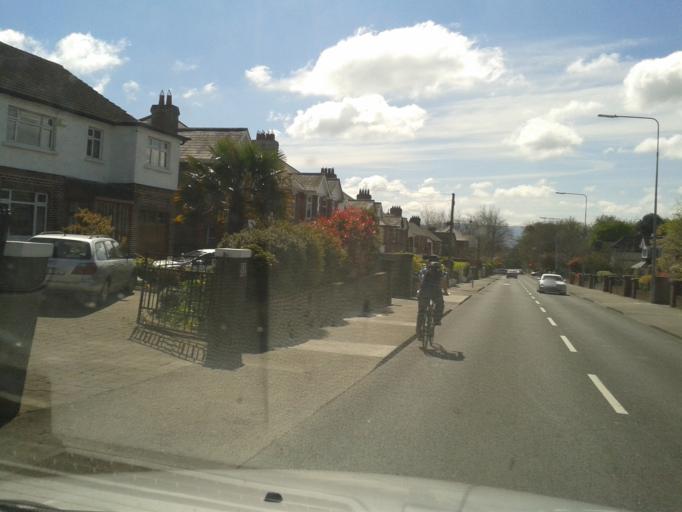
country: IE
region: Leinster
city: Marino
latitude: 53.3756
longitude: -6.2423
